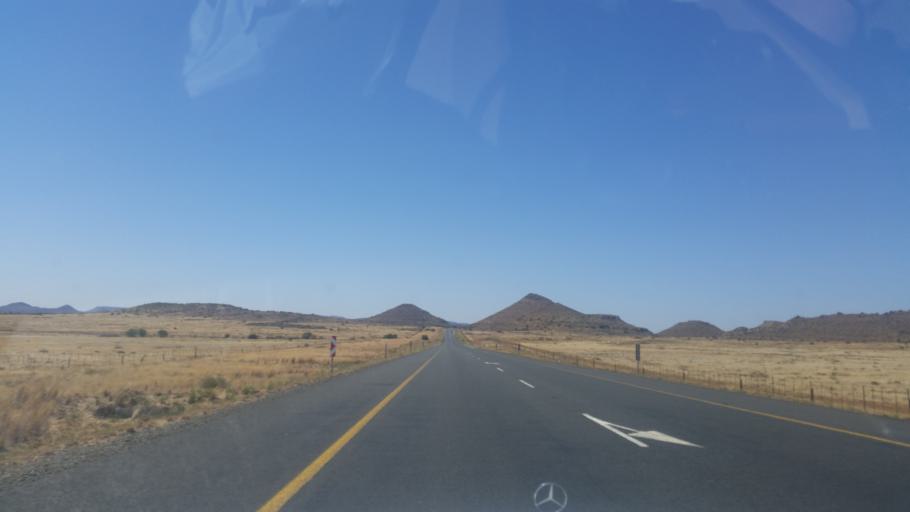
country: ZA
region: Northern Cape
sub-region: Pixley ka Seme District Municipality
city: Colesberg
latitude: -30.6083
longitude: 25.3853
